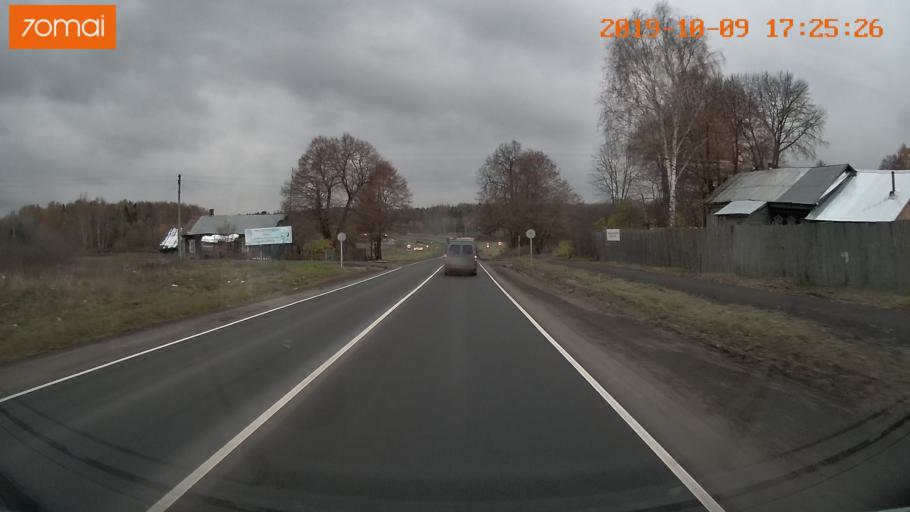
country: RU
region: Ivanovo
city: Furmanov
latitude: 57.1805
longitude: 41.0902
